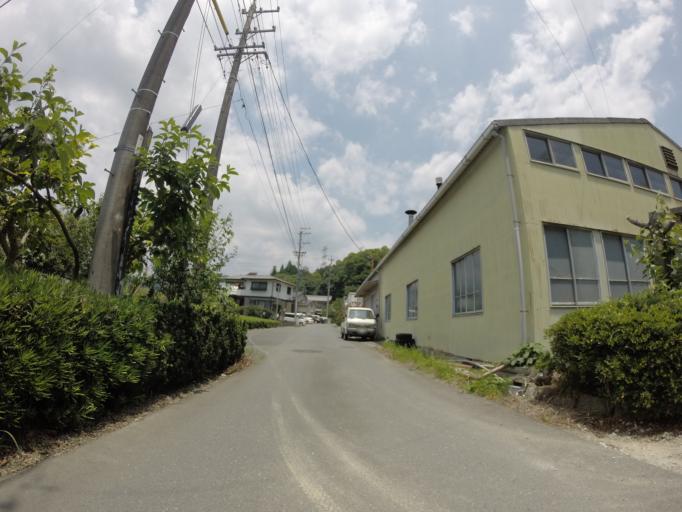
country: JP
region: Shizuoka
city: Kanaya
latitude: 34.8057
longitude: 138.0728
